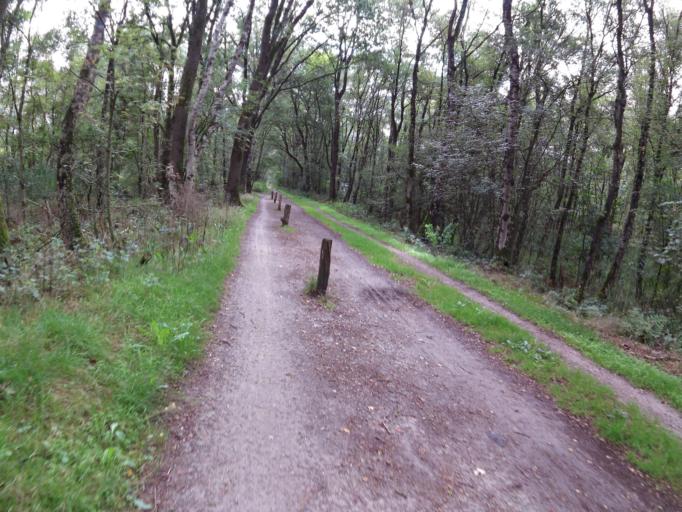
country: NL
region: Gelderland
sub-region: Berkelland
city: Eibergen
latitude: 52.0470
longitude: 6.6901
